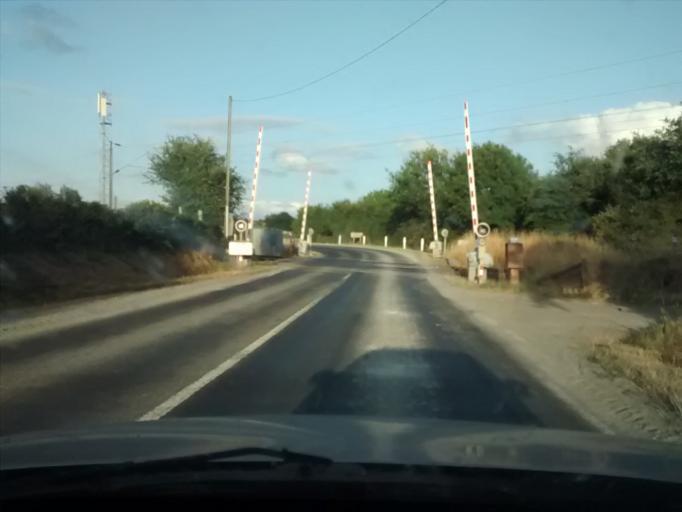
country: FR
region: Pays de la Loire
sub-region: Departement de la Sarthe
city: Sille-le-Guillaume
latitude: 48.1556
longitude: -0.2165
